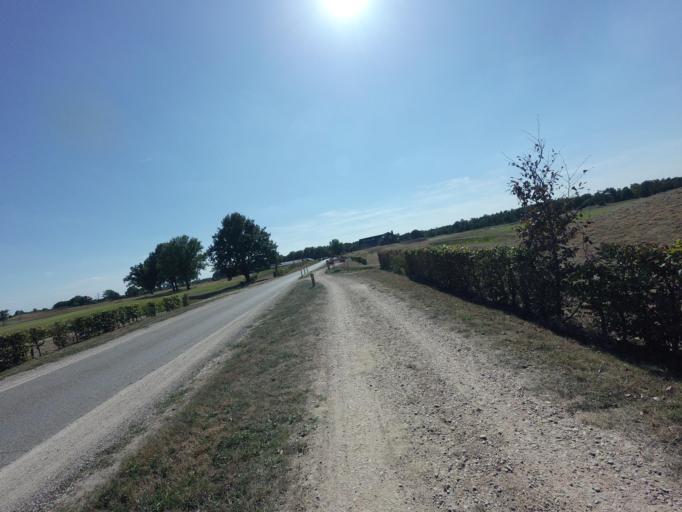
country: NL
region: North Brabant
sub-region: Gemeente Someren
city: Someren
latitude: 51.3760
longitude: 5.6691
